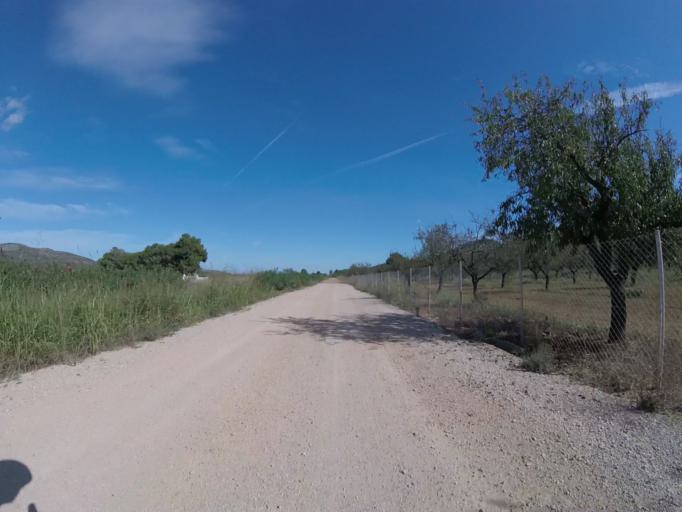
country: ES
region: Valencia
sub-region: Provincia de Castello
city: Santa Magdalena de Pulpis
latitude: 40.3785
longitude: 0.3339
